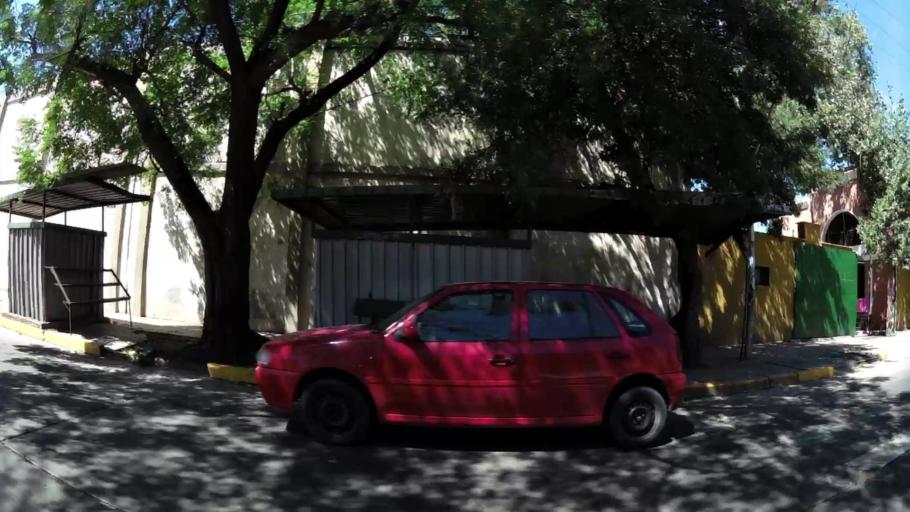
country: AR
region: Mendoza
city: Las Heras
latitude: -32.8573
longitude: -68.8376
